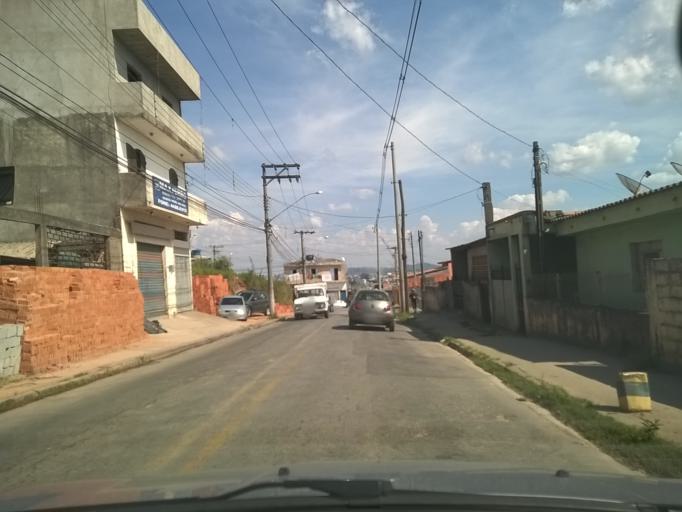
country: BR
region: Sao Paulo
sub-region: Francisco Morato
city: Francisco Morato
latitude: -23.2698
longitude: -46.7428
